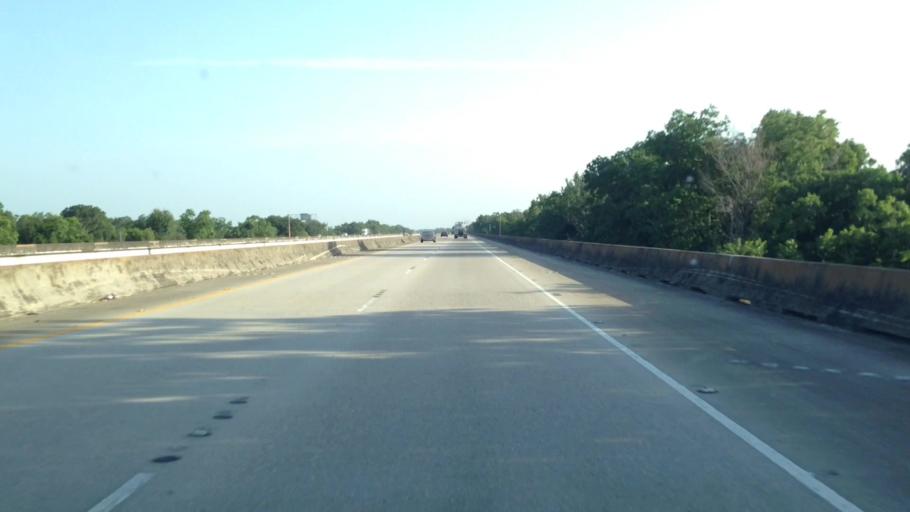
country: US
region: Louisiana
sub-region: Tangipahoa Parish
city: Ponchatoula
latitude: 30.3255
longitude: -90.4096
